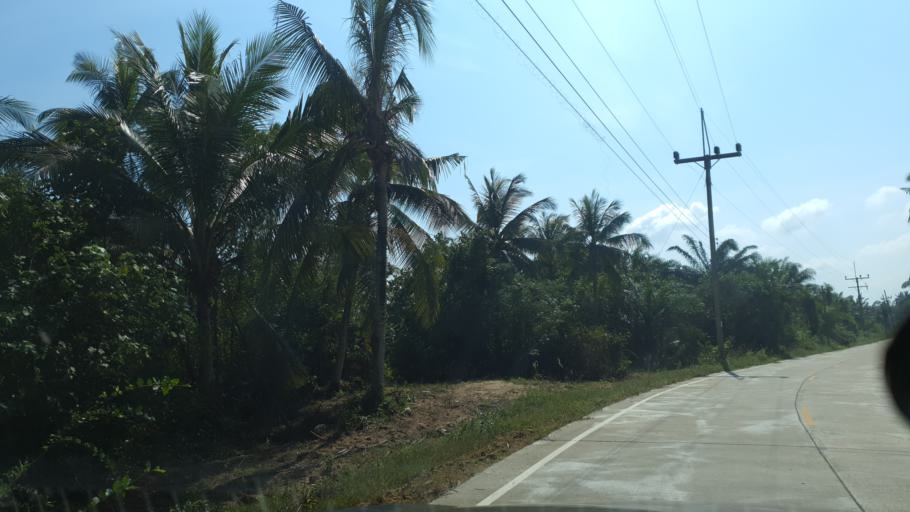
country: TH
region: Surat Thani
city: Tha Chana
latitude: 9.5946
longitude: 99.2048
